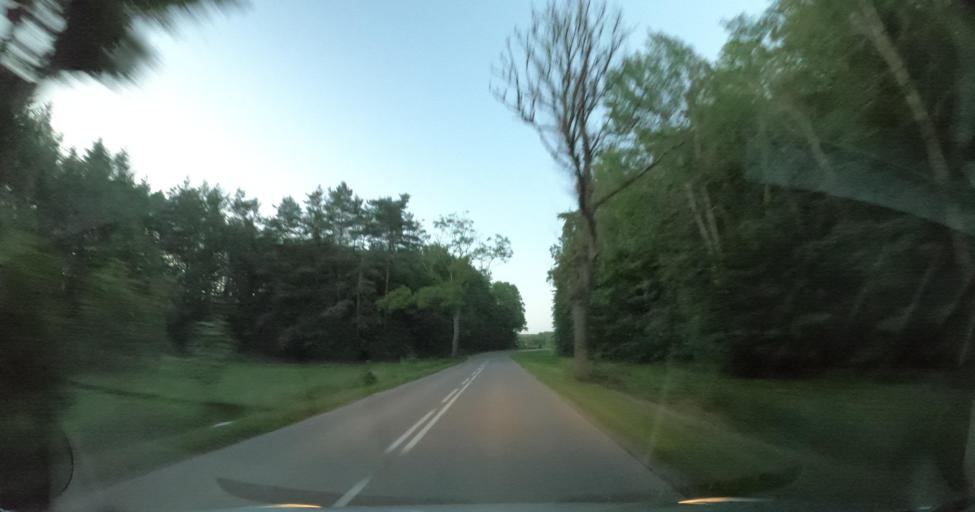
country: PL
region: Pomeranian Voivodeship
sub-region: Powiat wejherowski
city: Koleczkowo
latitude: 54.4684
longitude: 18.2892
